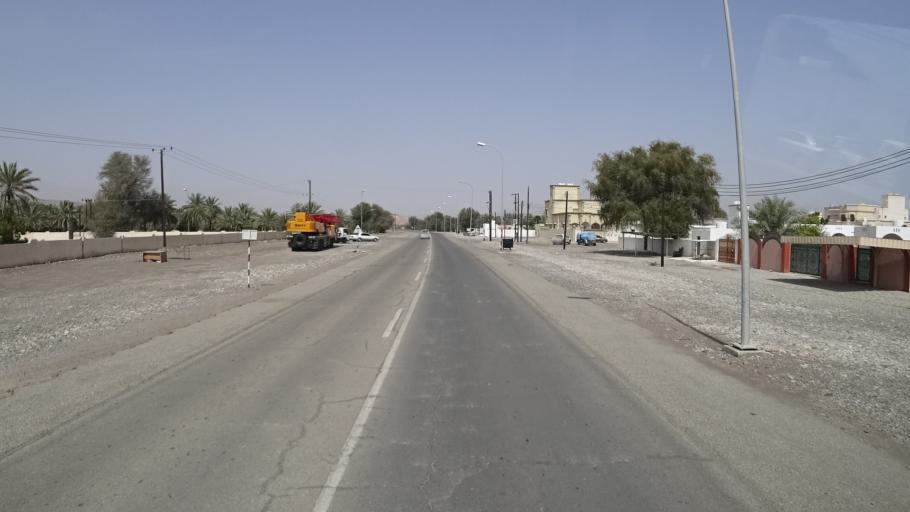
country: OM
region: Muhafazat Masqat
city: Muscat
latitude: 23.2060
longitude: 58.9660
